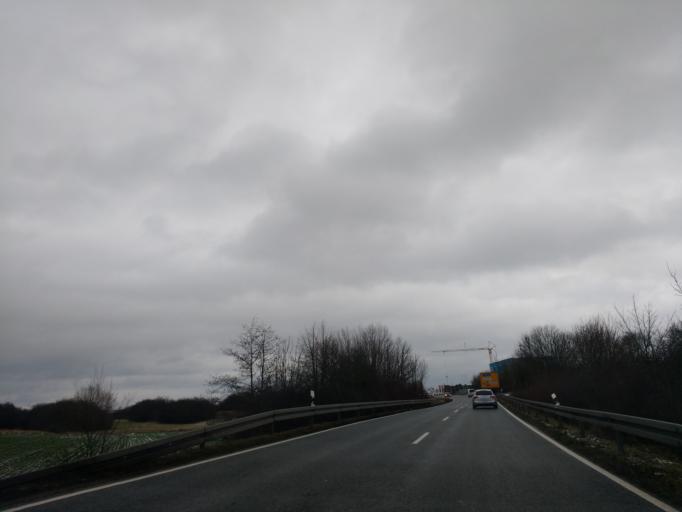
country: DE
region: Bavaria
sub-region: Regierungsbezirk Mittelfranken
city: Herzogenaurach
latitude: 49.5811
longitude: 10.8774
